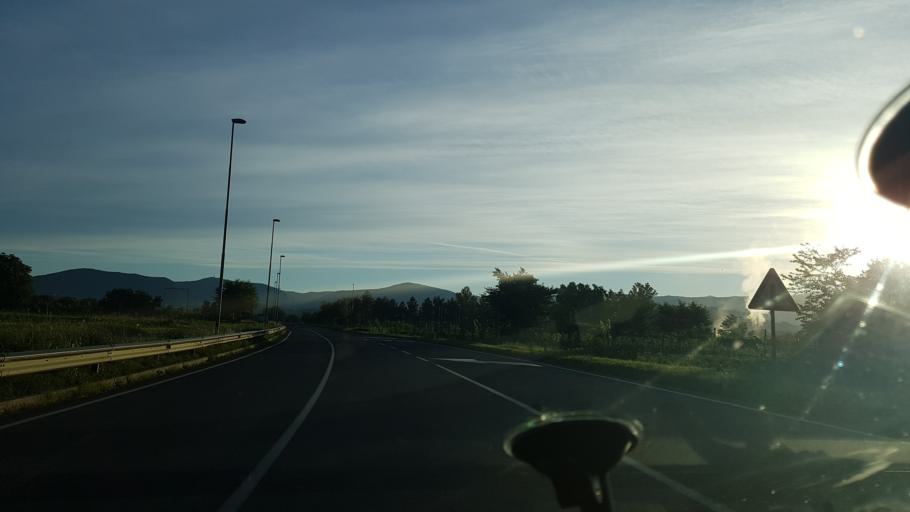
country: SI
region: Sempeter-Vrtojba
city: Vrtojba
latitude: 45.9082
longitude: 13.6261
